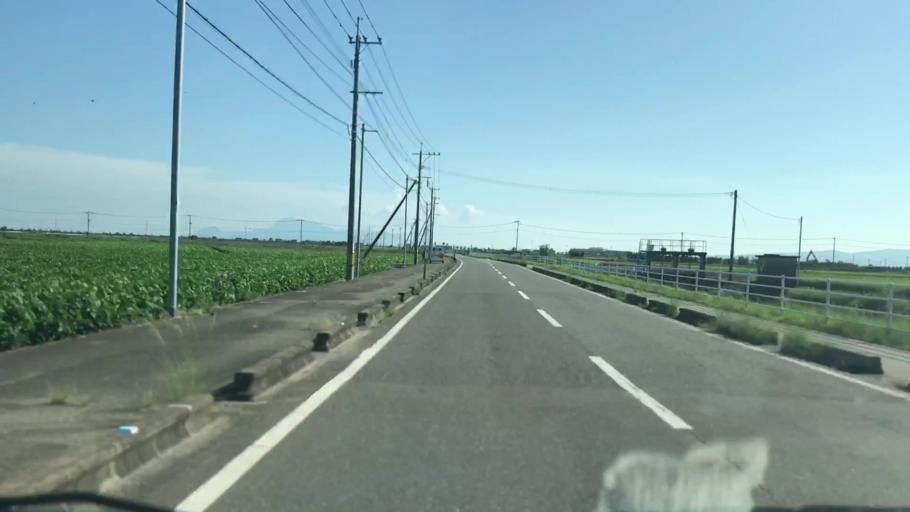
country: JP
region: Saga Prefecture
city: Okawa
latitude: 33.1673
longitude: 130.3095
